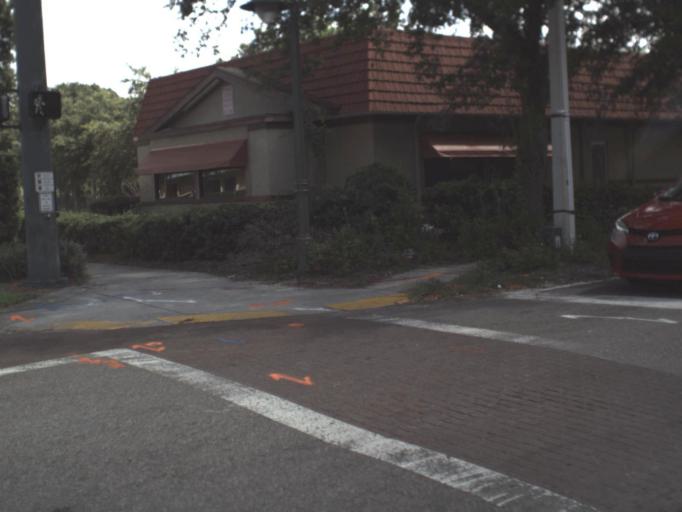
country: US
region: Florida
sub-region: Pinellas County
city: Belleair
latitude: 27.9241
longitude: -82.7963
